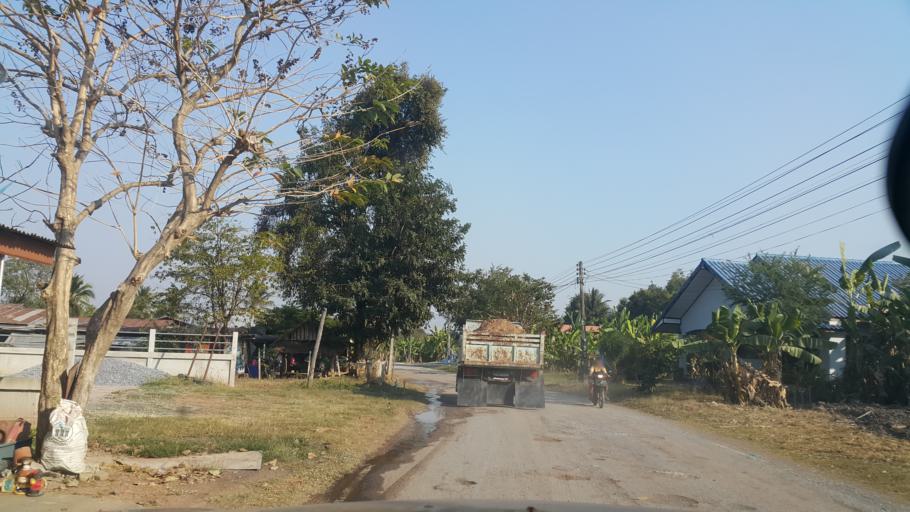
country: TH
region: Nakhon Ratchasima
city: Chakkarat
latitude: 15.0685
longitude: 102.3970
